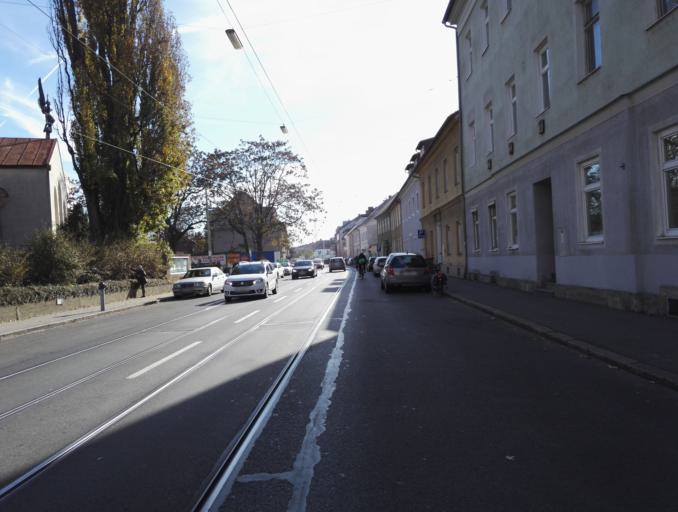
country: AT
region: Styria
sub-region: Graz Stadt
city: Graz
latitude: 47.0616
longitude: 15.4517
